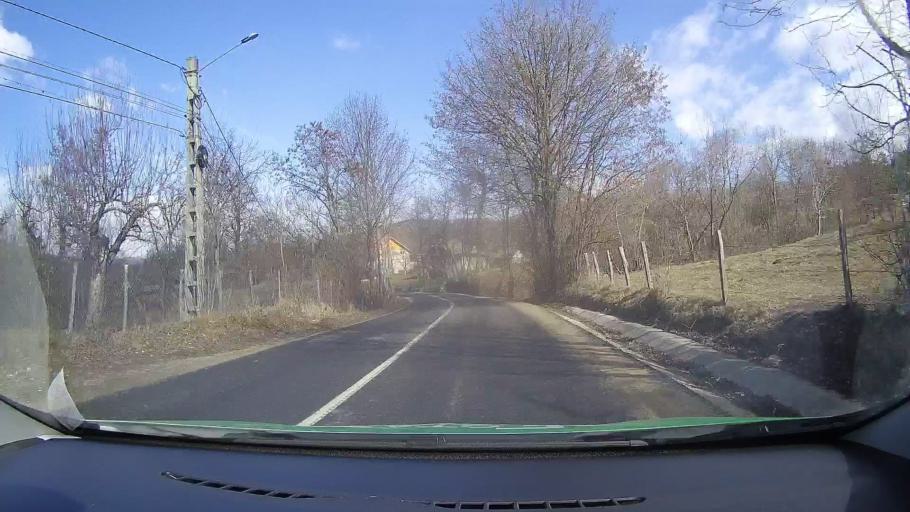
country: RO
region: Dambovita
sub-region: Comuna Runcu
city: Badeni
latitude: 45.1432
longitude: 25.4043
